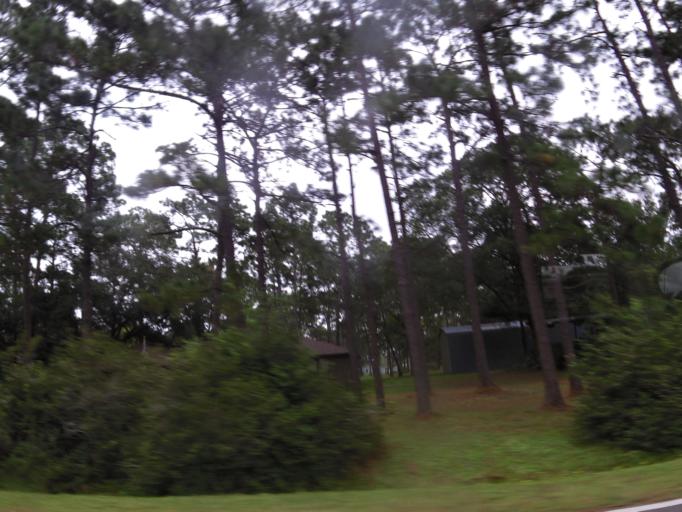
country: US
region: Florida
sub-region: Clay County
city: Bellair-Meadowbrook Terrace
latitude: 30.2183
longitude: -81.7727
